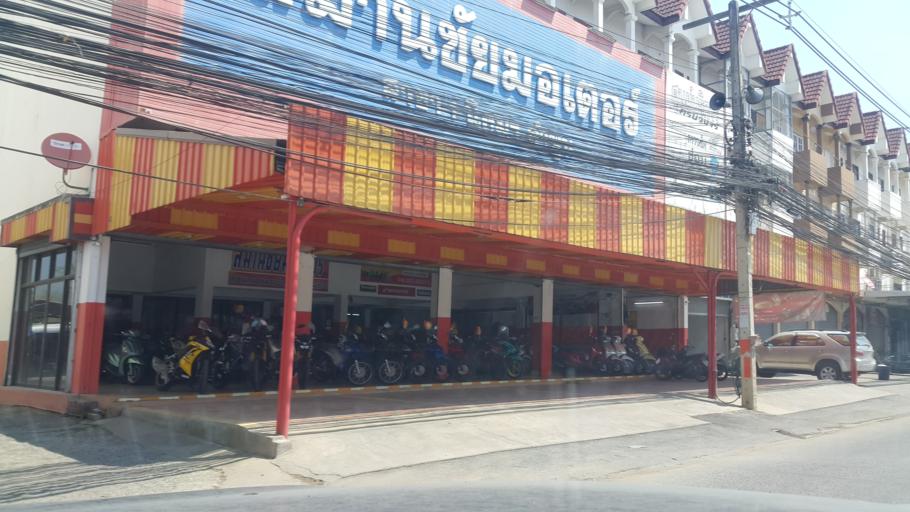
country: TH
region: Lamphun
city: Lamphun
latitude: 18.5931
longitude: 99.0360
